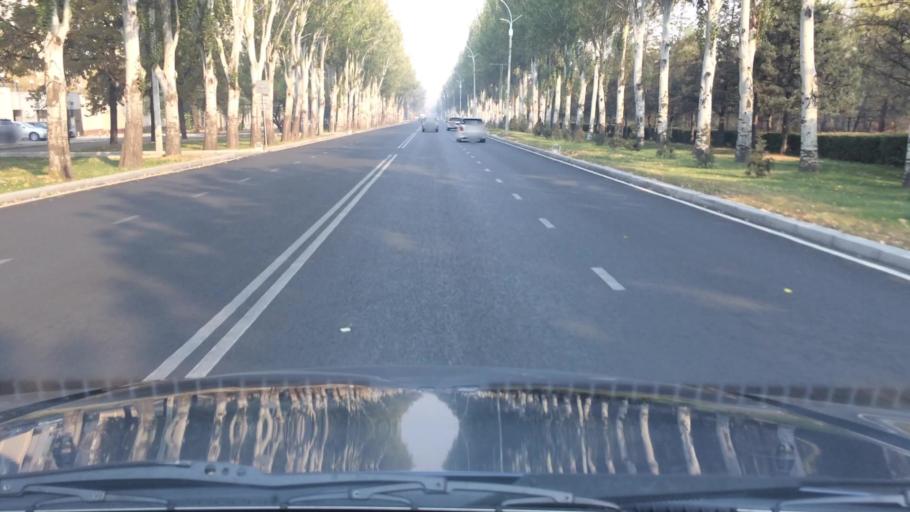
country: KG
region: Chuy
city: Bishkek
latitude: 42.8342
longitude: 74.5855
